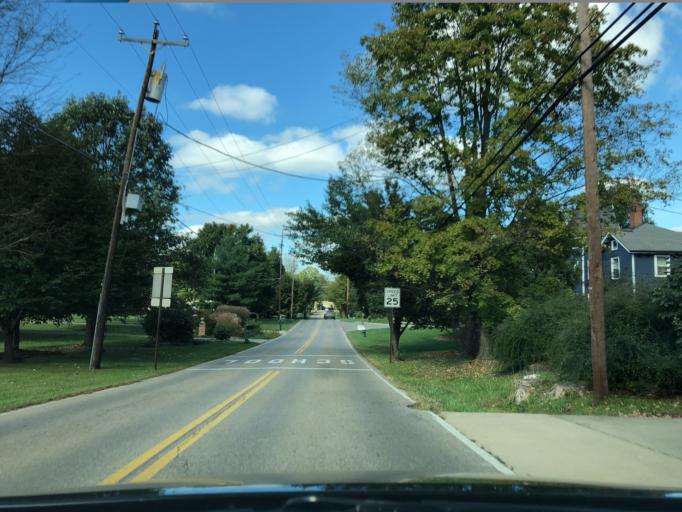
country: US
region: Ohio
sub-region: Hamilton County
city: Loveland
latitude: 39.2556
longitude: -84.2500
